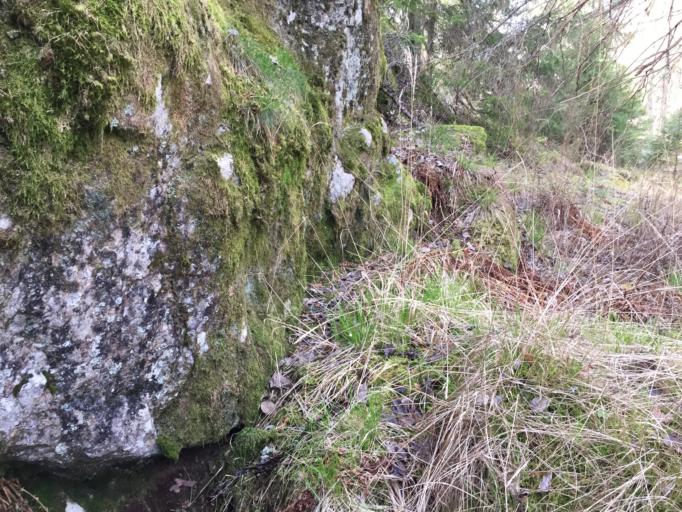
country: SE
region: Stockholm
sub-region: Salems Kommun
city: Ronninge
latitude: 59.2515
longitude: 17.6902
